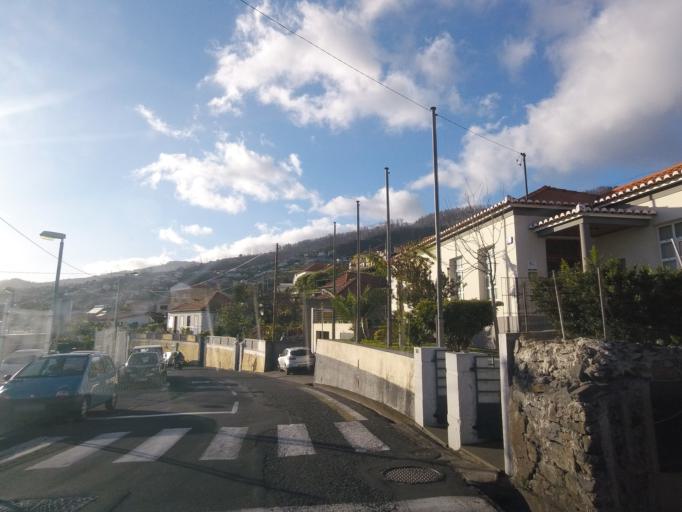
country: PT
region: Madeira
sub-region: Funchal
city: Nossa Senhora do Monte
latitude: 32.6711
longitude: -16.9220
